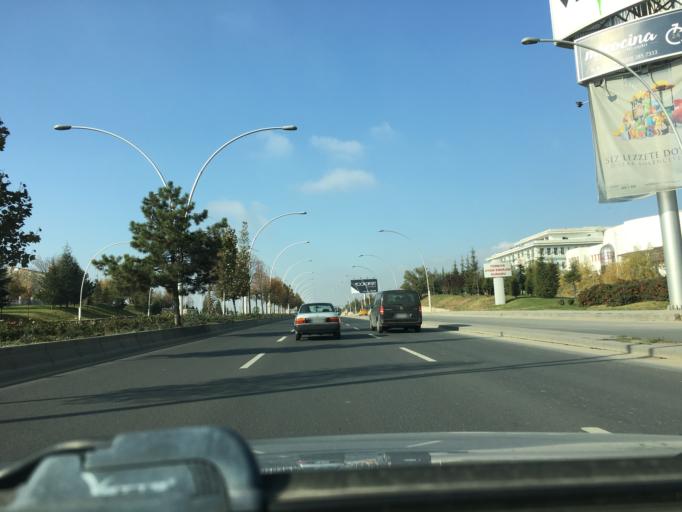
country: TR
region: Ankara
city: Batikent
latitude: 39.9070
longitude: 32.7440
